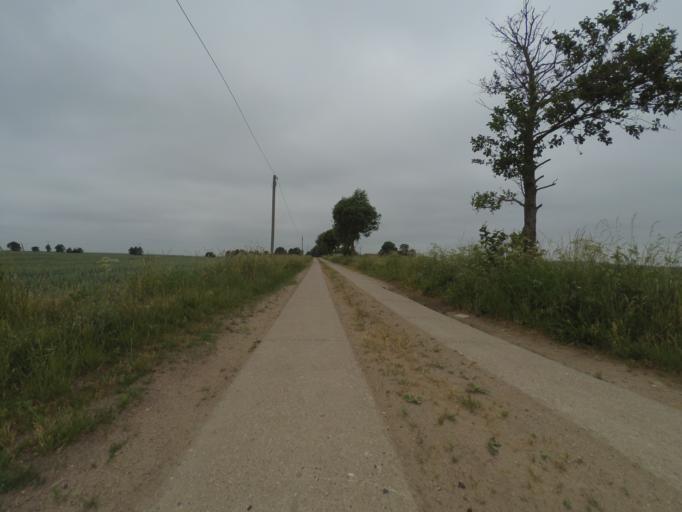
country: DE
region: Mecklenburg-Vorpommern
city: Dabel
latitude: 53.6705
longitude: 11.9294
